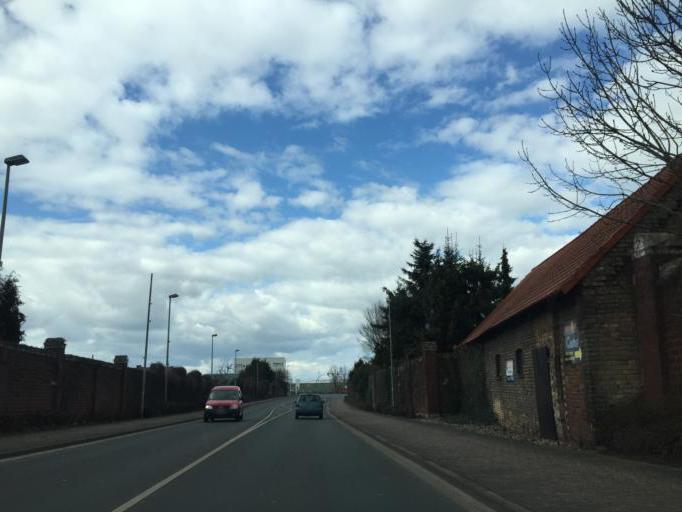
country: DE
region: Lower Saxony
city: Peine
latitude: 52.3504
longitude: 10.2426
